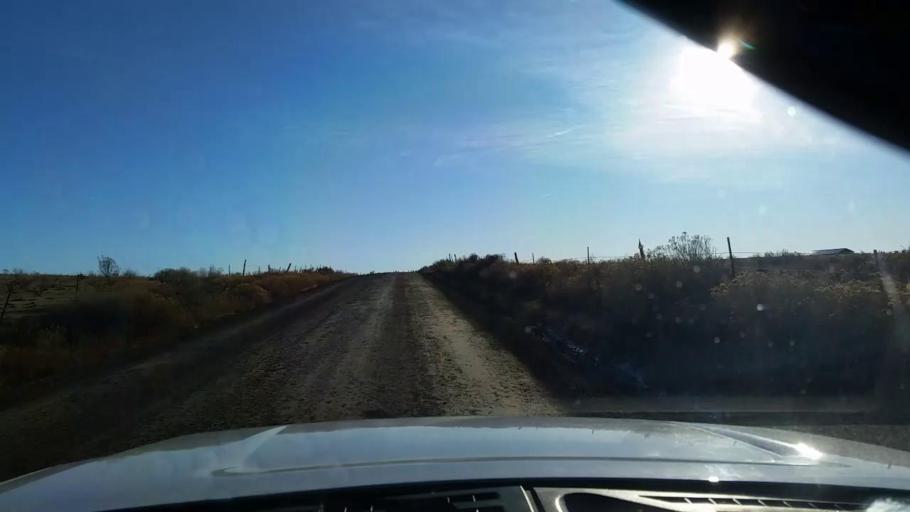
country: US
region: Colorado
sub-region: Larimer County
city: Wellington
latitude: 40.7701
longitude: -105.1168
